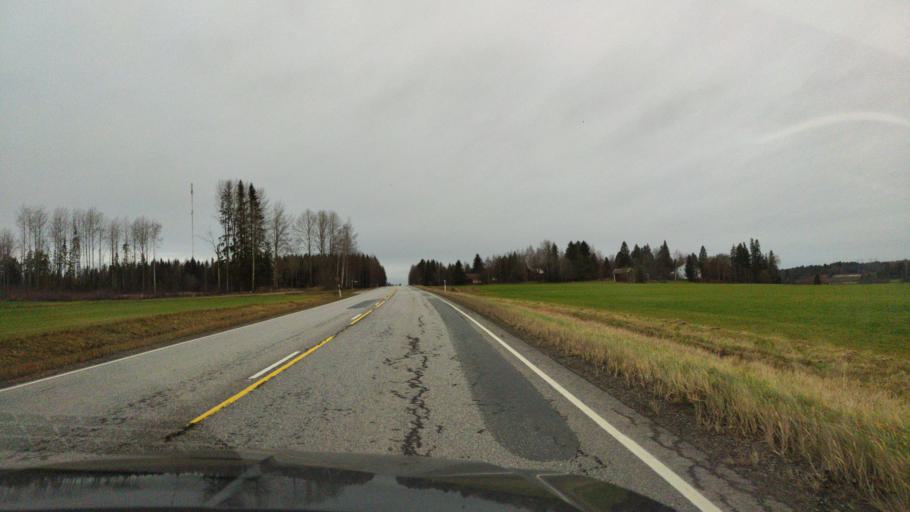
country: FI
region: Varsinais-Suomi
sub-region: Loimaa
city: Ylaene
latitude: 60.8529
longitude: 22.4319
